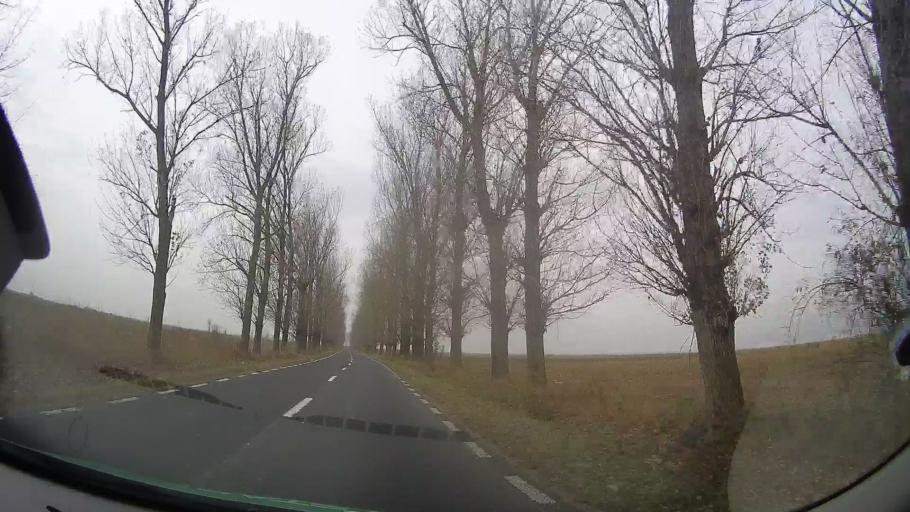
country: RO
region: Ilfov
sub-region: Comuna Nuci
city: Nuci
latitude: 44.7220
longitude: 26.2821
